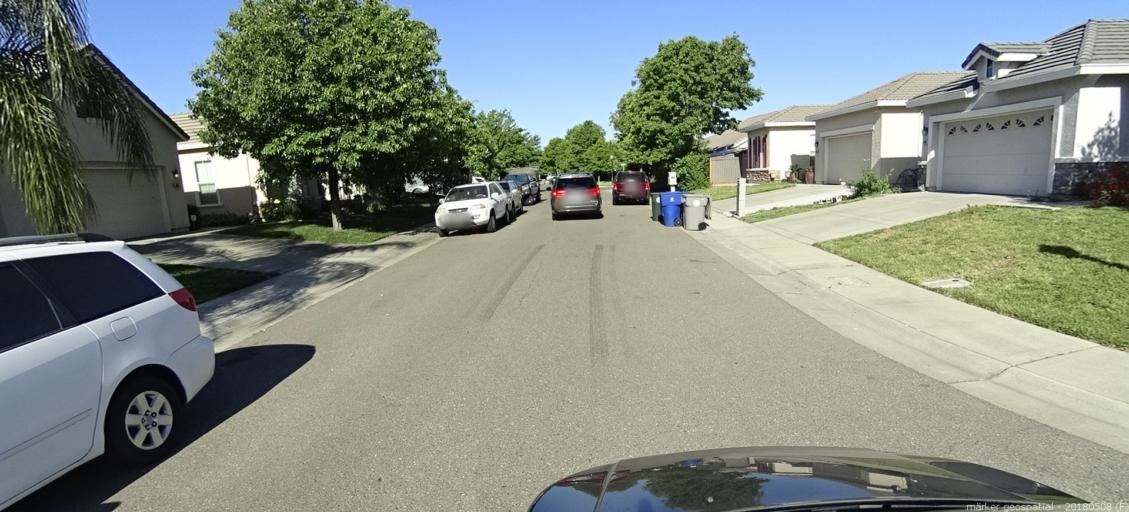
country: US
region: California
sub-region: Sacramento County
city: Elverta
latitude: 38.6799
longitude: -121.4968
